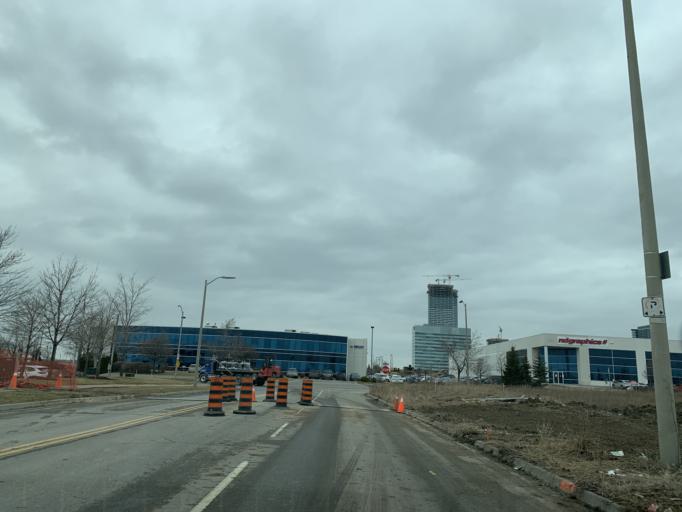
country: CA
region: Ontario
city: Concord
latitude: 43.7884
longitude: -79.5283
